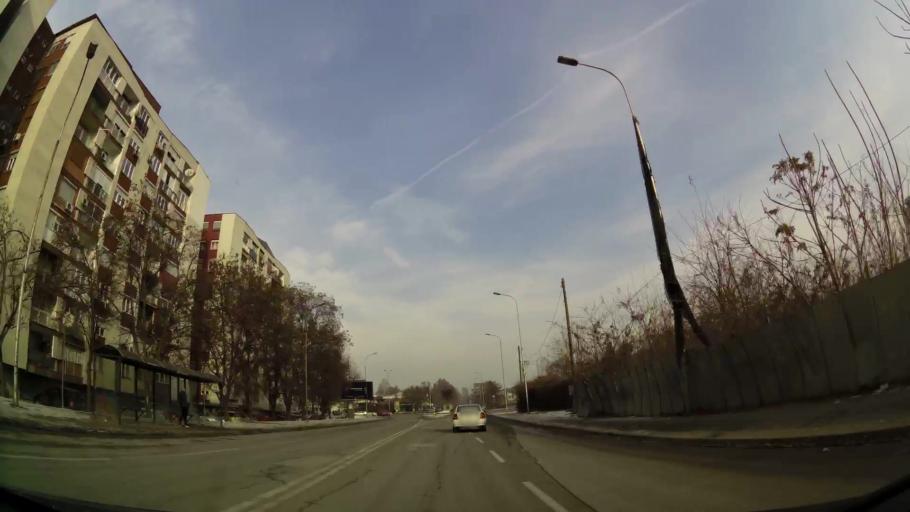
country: MK
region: Cair
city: Cair
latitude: 42.0214
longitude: 21.4338
